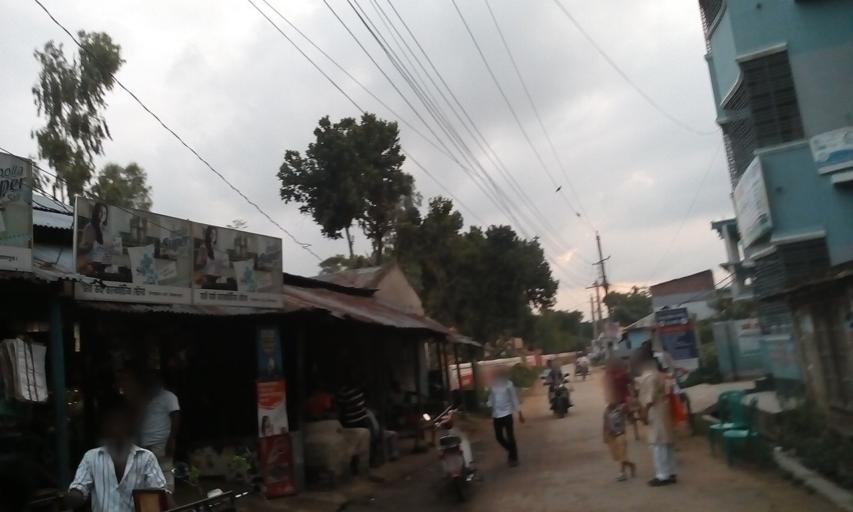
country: IN
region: West Bengal
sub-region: Dakshin Dinajpur
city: Balurghat
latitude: 25.3808
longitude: 88.9930
